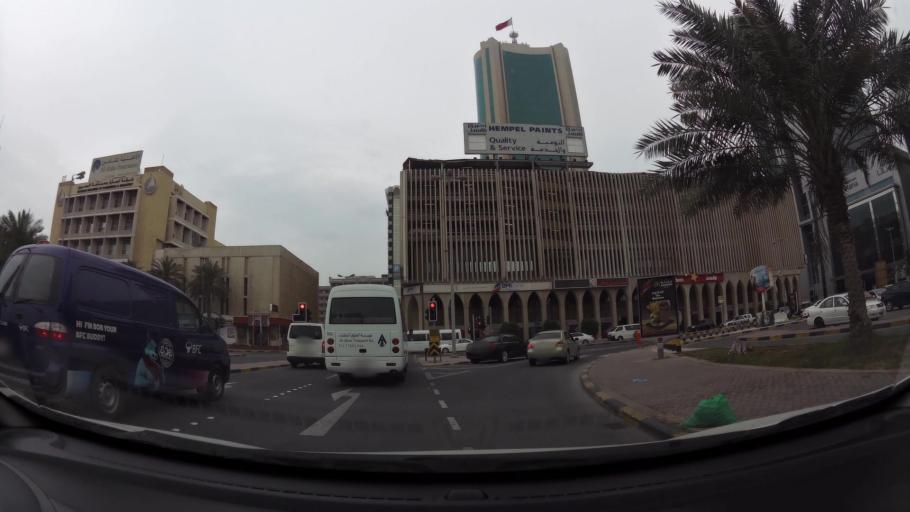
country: BH
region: Manama
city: Manama
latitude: 26.2358
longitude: 50.5755
